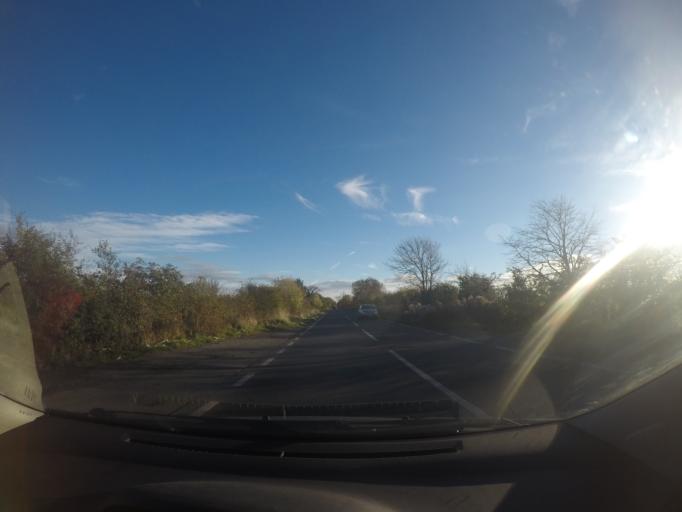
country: GB
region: England
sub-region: City of York
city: York
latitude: 53.9862
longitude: -1.0847
